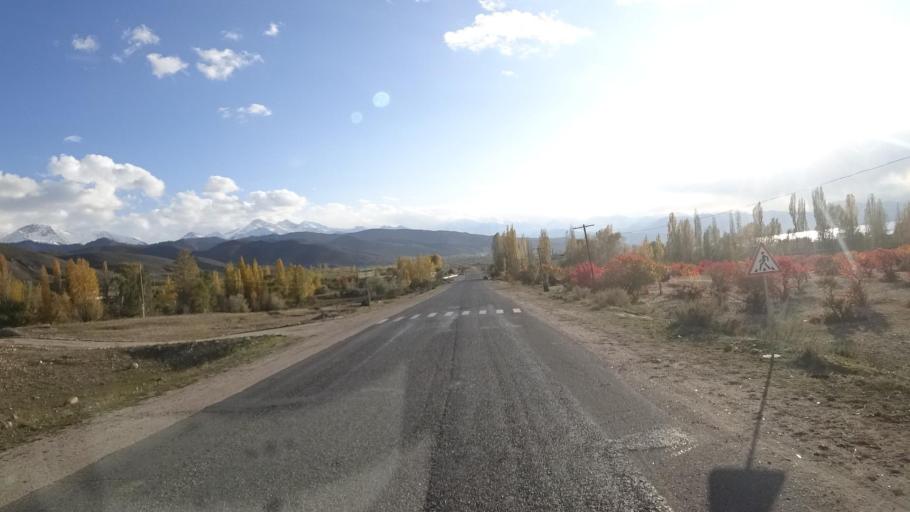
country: KG
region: Ysyk-Koel
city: Pokrovka
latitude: 42.2258
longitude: 77.7130
